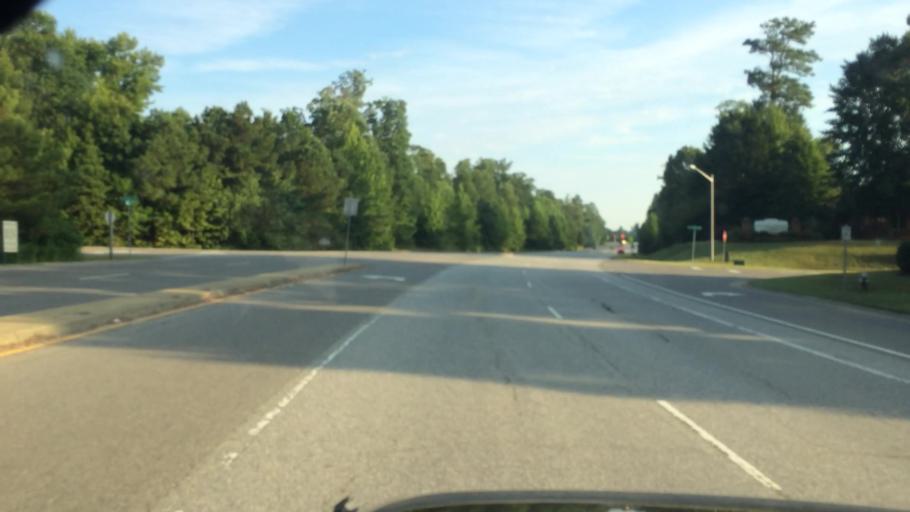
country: US
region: Virginia
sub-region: James City County
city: Williamsburg
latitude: 37.3332
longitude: -76.7358
